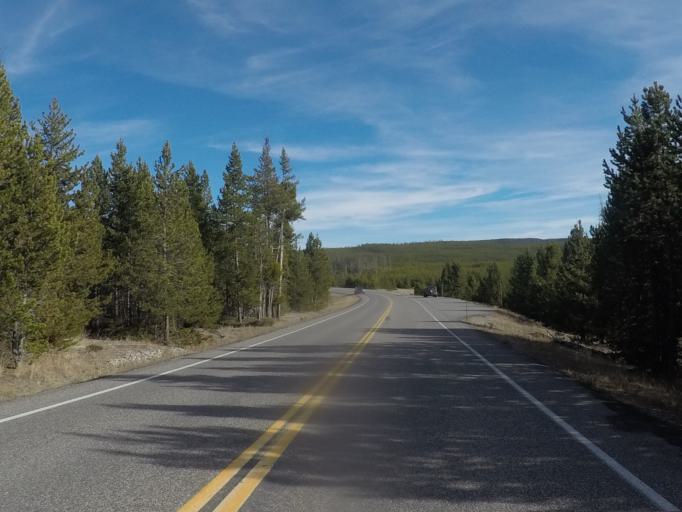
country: US
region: Montana
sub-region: Gallatin County
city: West Yellowstone
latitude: 44.6490
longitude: -110.8439
